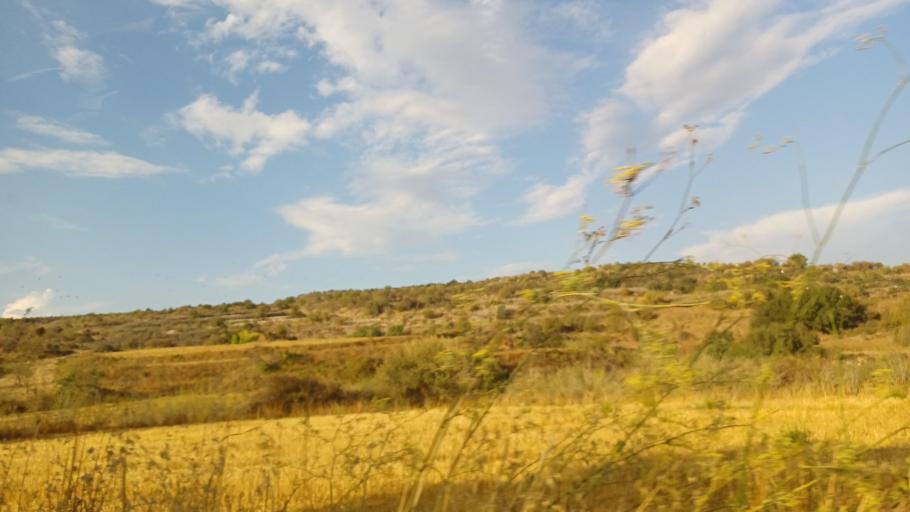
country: CY
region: Pafos
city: Tala
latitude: 34.9107
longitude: 32.5007
